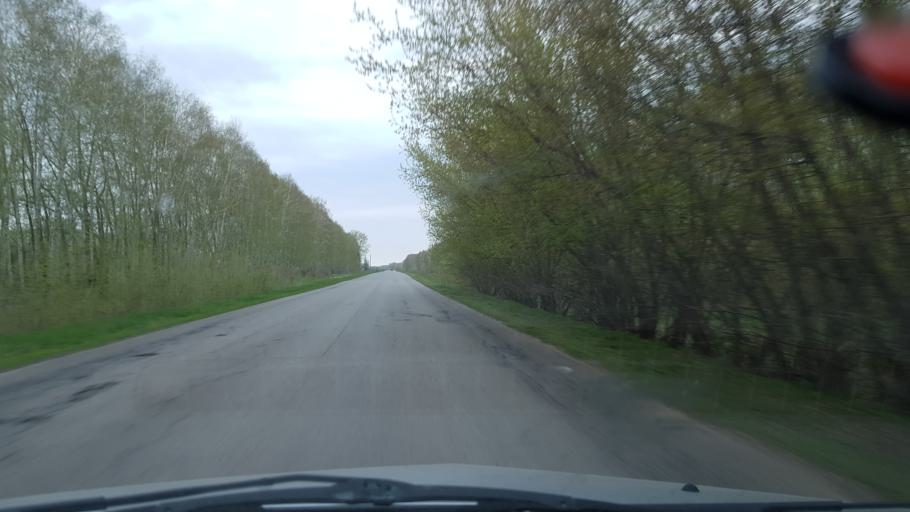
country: RU
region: Samara
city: Podstepki
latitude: 53.6652
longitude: 49.1728
